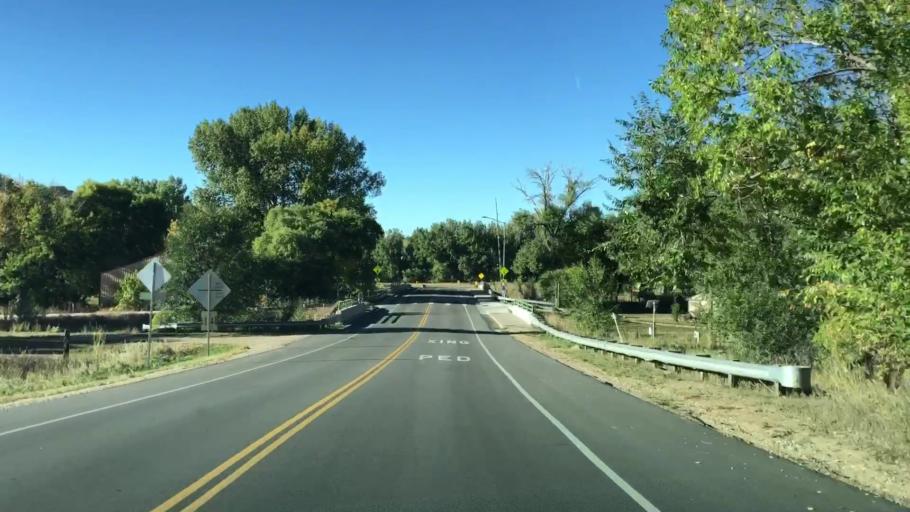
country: US
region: Colorado
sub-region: Larimer County
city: Loveland
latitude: 40.4059
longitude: -105.1407
